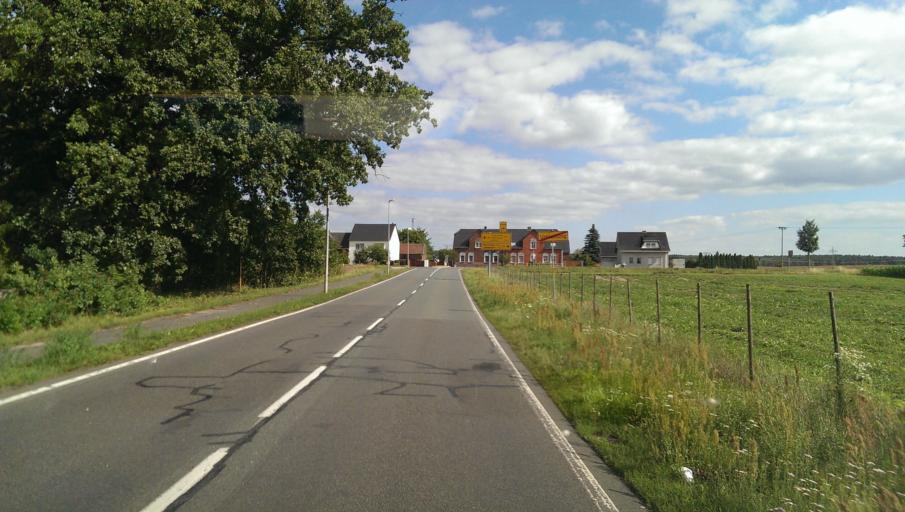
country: DE
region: Saxony-Anhalt
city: Radis
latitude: 51.7512
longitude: 12.5102
